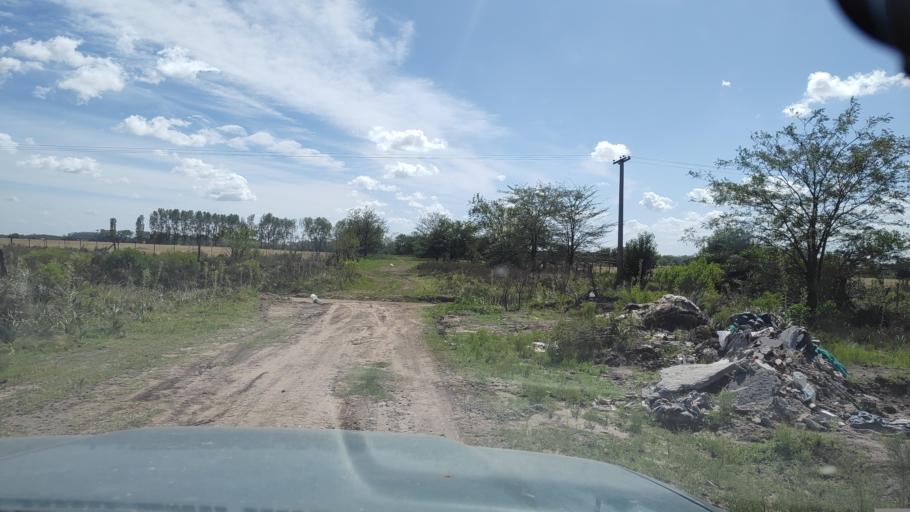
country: AR
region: Buenos Aires
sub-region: Partido de Lujan
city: Lujan
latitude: -34.5176
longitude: -59.1617
